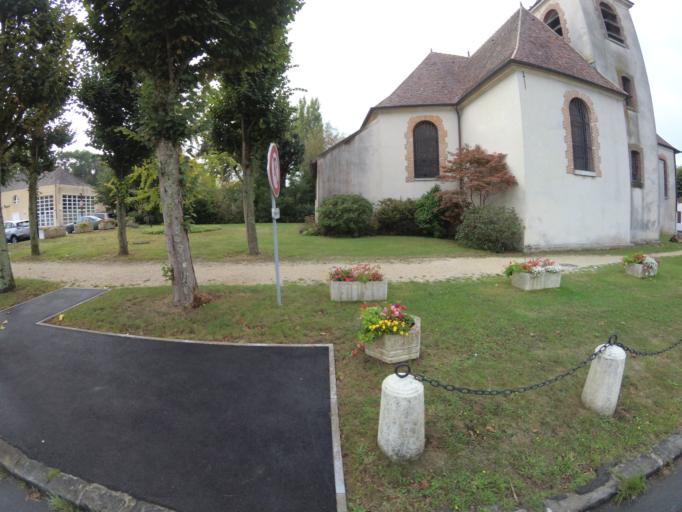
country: FR
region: Ile-de-France
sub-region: Departement de Seine-et-Marne
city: Guermantes
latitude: 48.8547
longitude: 2.7052
